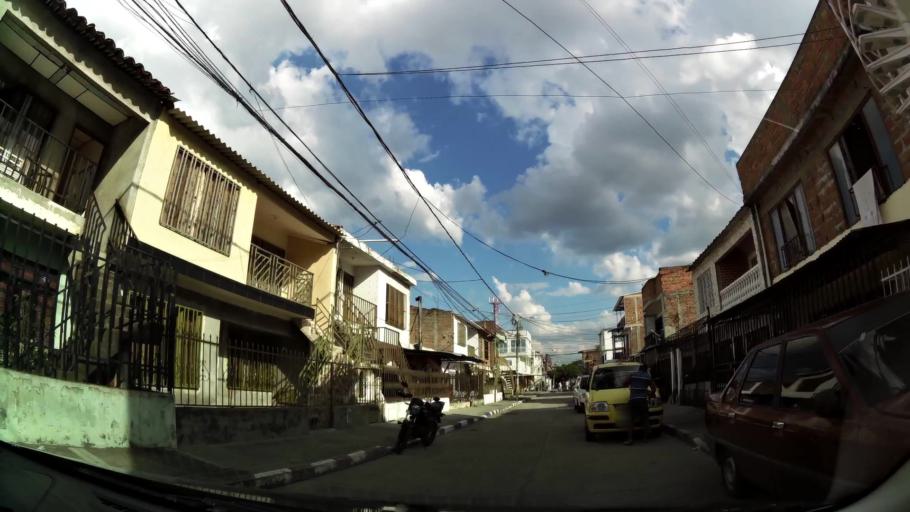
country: CO
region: Valle del Cauca
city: Cali
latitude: 3.4041
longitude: -76.5121
